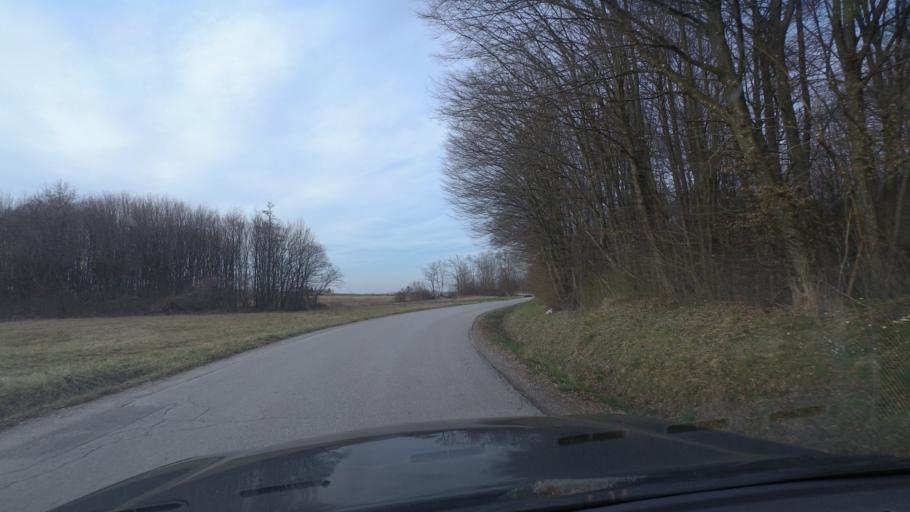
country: HR
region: Grad Zagreb
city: Horvati
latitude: 45.7087
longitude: 15.8258
